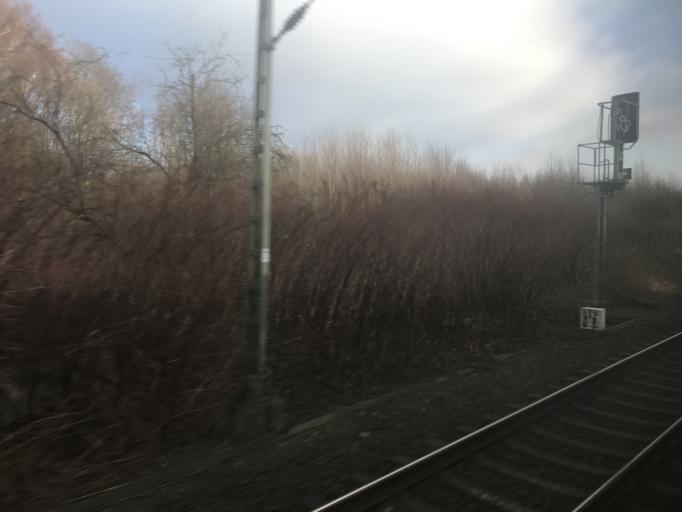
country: DE
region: North Rhine-Westphalia
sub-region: Regierungsbezirk Arnsberg
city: Bochum
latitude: 51.4853
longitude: 7.2897
